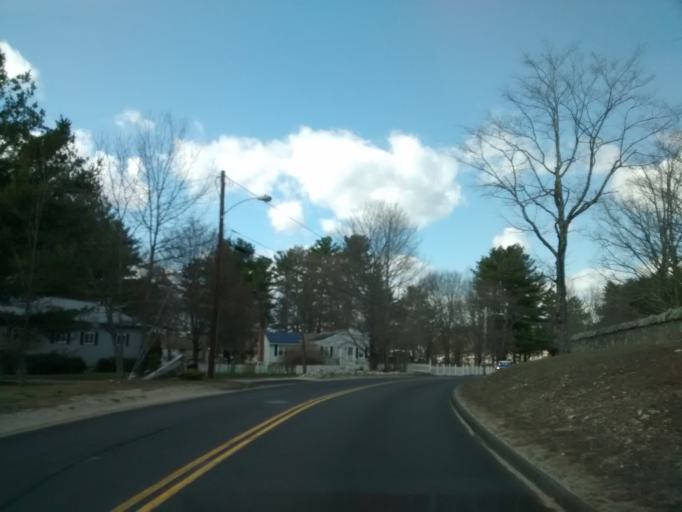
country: US
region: Massachusetts
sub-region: Worcester County
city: Upton
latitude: 42.1622
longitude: -71.6207
